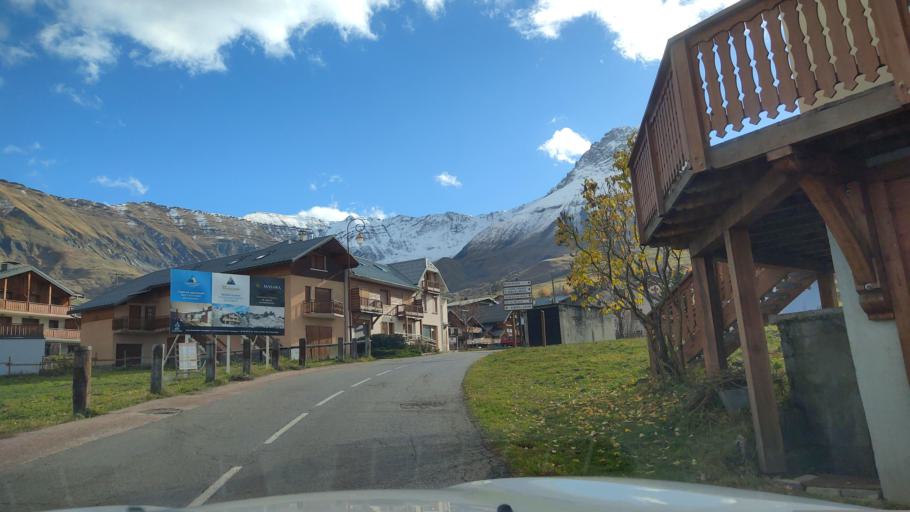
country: FR
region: Rhone-Alpes
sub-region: Departement de la Savoie
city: Villargondran
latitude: 45.2189
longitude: 6.3395
